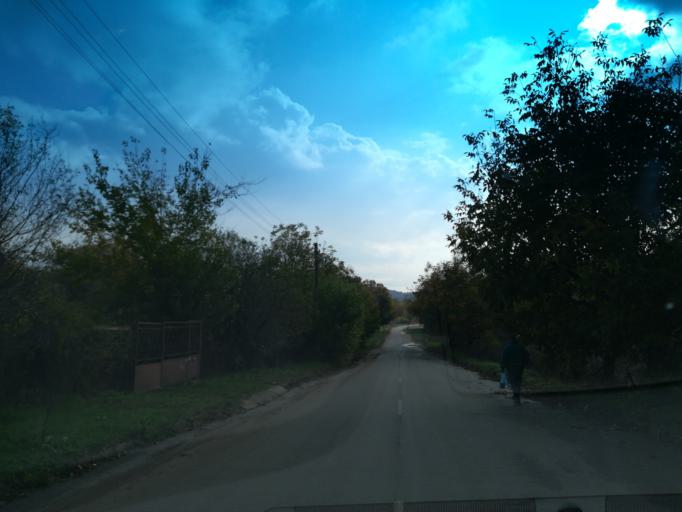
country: BG
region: Stara Zagora
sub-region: Obshtina Nikolaevo
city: Elkhovo
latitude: 42.3400
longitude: 25.4041
